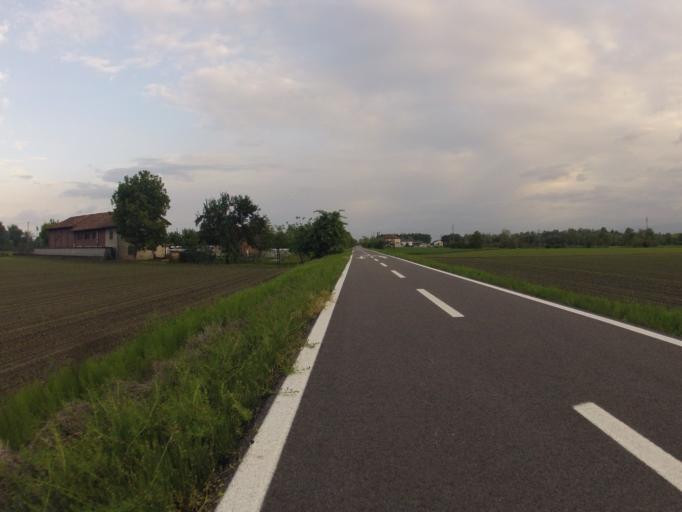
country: IT
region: Piedmont
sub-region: Provincia di Torino
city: Vigone
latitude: 44.8182
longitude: 7.4974
